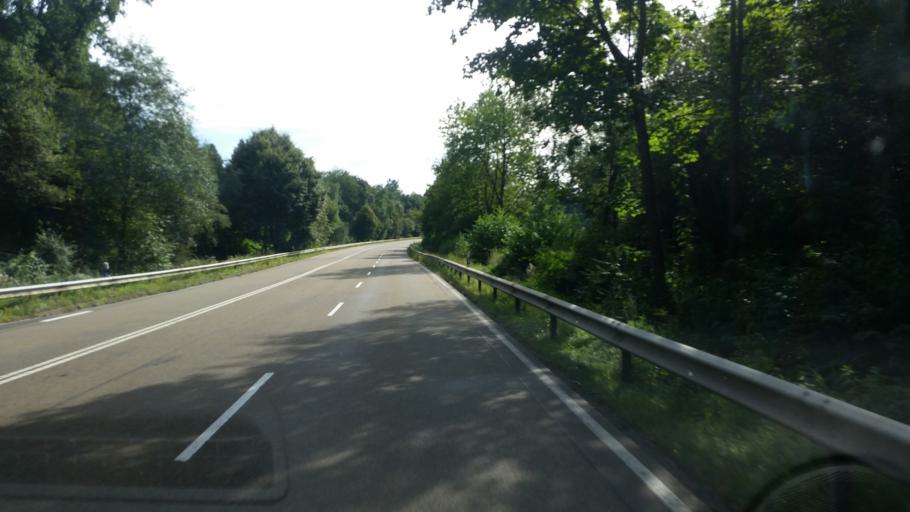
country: DE
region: Rheinland-Pfalz
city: Eitelborn
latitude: 50.3677
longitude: 7.6909
